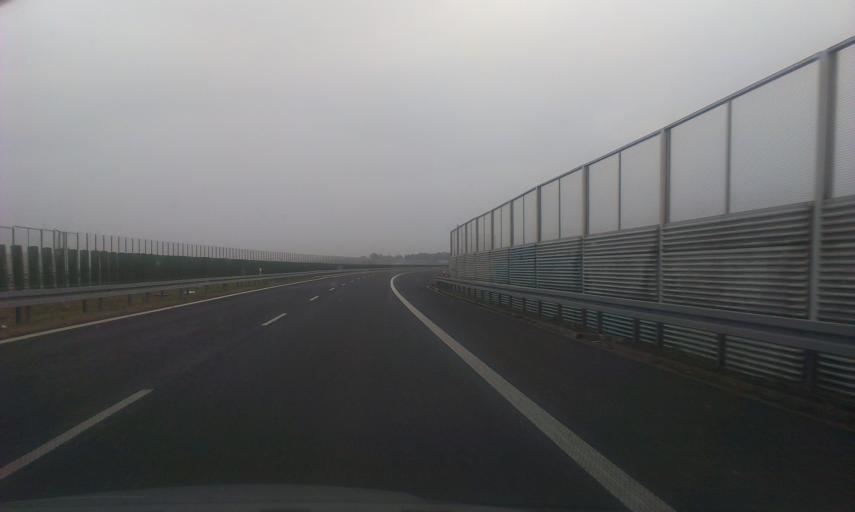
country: PL
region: Greater Poland Voivodeship
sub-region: Powiat poznanski
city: Rokietnica
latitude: 52.5130
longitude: 16.7856
